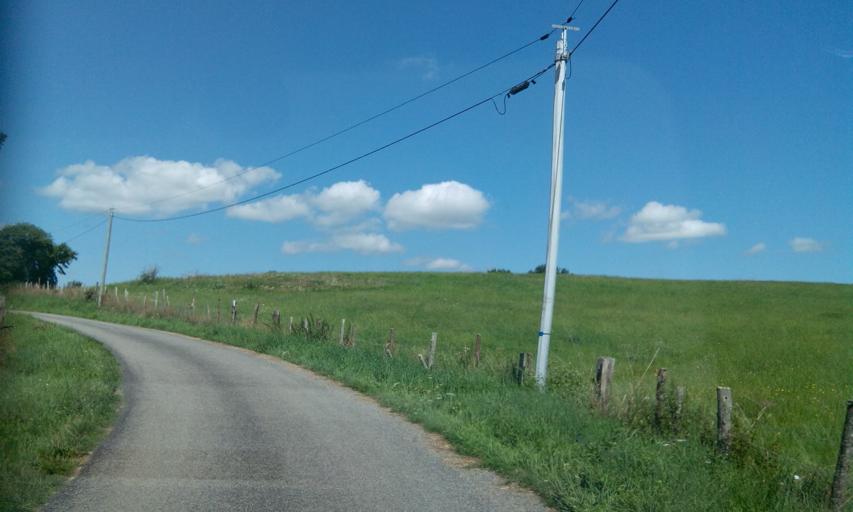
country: FR
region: Limousin
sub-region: Departement de la Haute-Vienne
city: Saint-Leonard-de-Noblat
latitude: 45.8165
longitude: 1.4757
